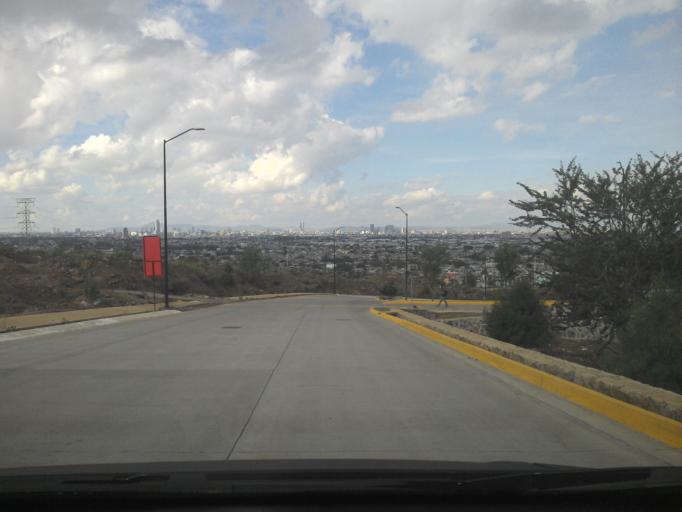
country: MX
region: Jalisco
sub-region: Tlajomulco de Zuniga
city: Altus Bosques
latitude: 20.6117
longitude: -103.3637
